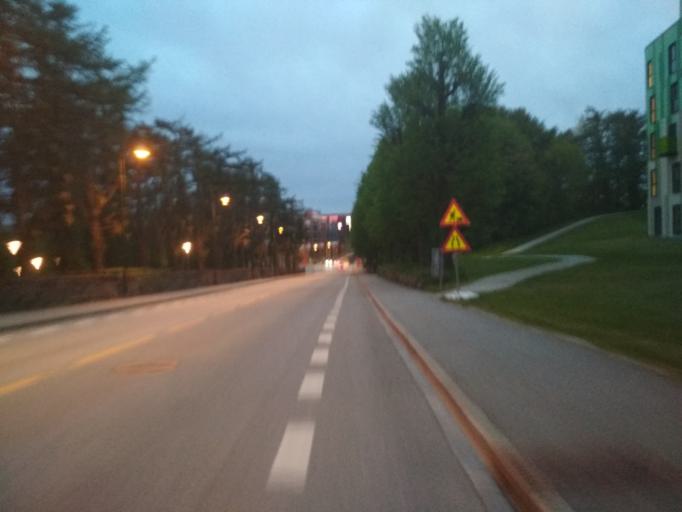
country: NO
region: Rogaland
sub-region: Stavanger
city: Stavanger
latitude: 58.9764
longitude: 5.7177
